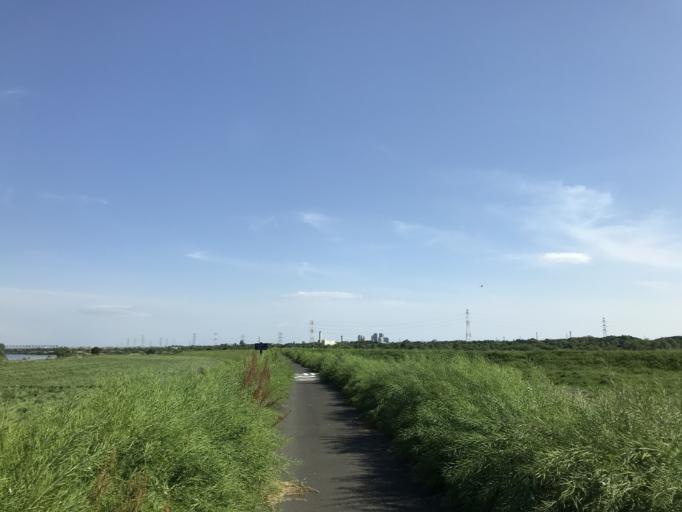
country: JP
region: Ibaraki
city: Moriya
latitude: 35.9454
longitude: 139.9426
